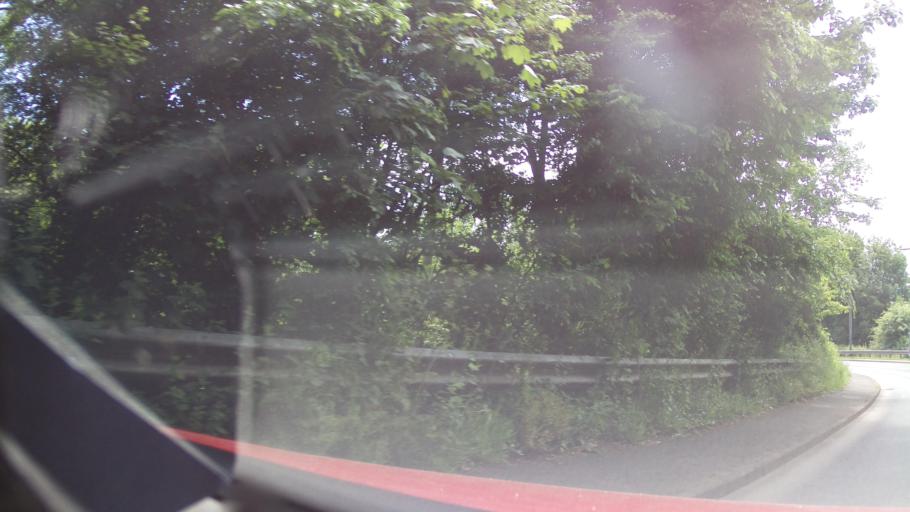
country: GB
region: England
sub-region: Devon
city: Cullompton
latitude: 50.8594
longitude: -3.3817
